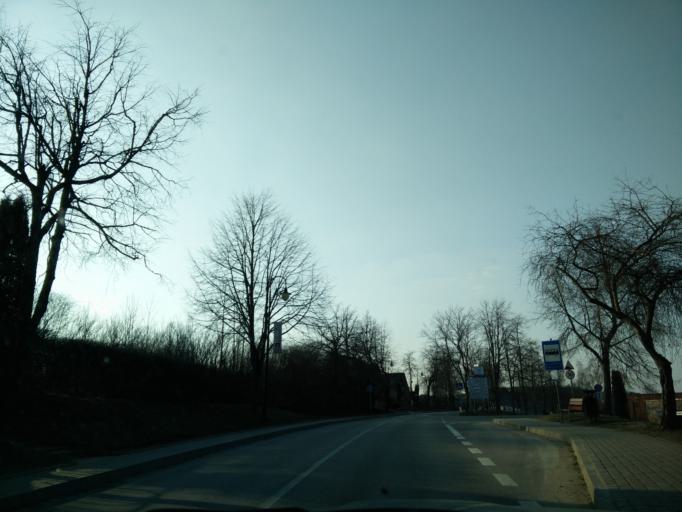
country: LT
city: Trakai
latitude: 54.6512
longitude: 24.9231
